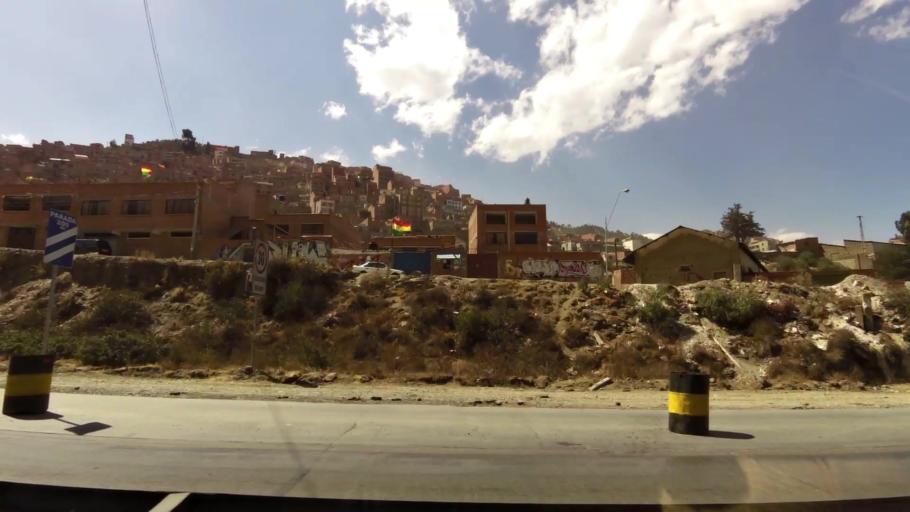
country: BO
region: La Paz
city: La Paz
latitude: -16.4826
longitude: -68.1478
